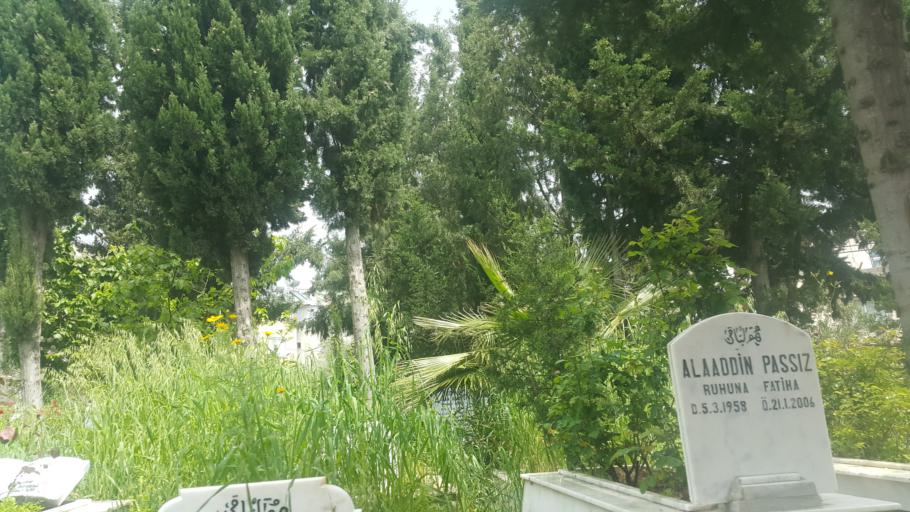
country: TR
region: Mersin
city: Mercin
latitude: 36.8210
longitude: 34.6032
